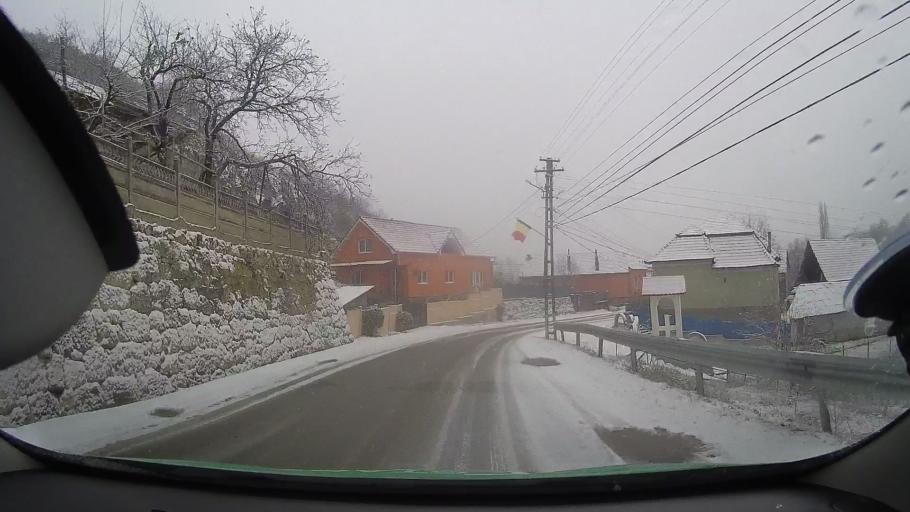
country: RO
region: Alba
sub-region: Comuna Livezile
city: Livezile
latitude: 46.3478
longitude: 23.6395
